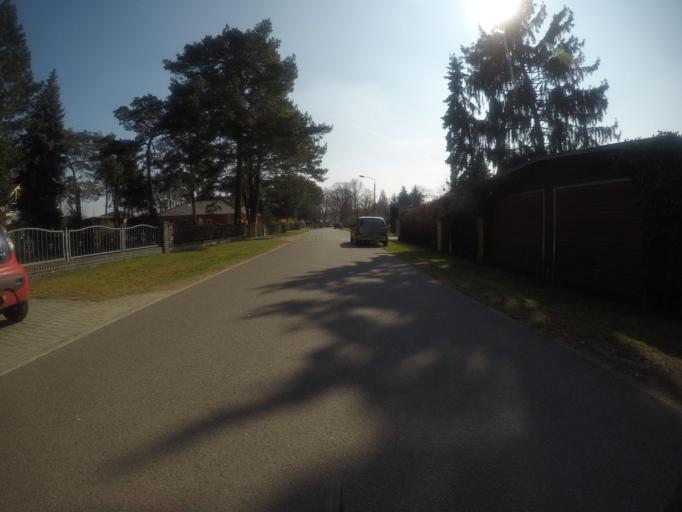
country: DE
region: Brandenburg
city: Konigs Wusterhausen
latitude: 52.2944
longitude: 13.6793
